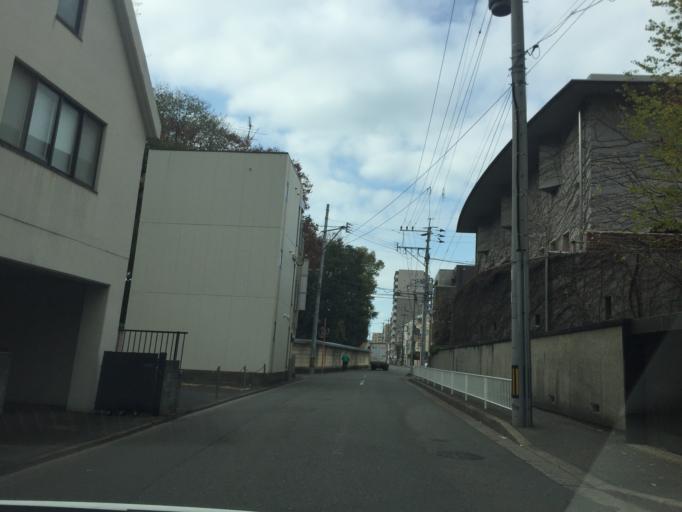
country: JP
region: Fukuoka
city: Fukuoka-shi
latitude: 33.6147
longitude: 130.4248
